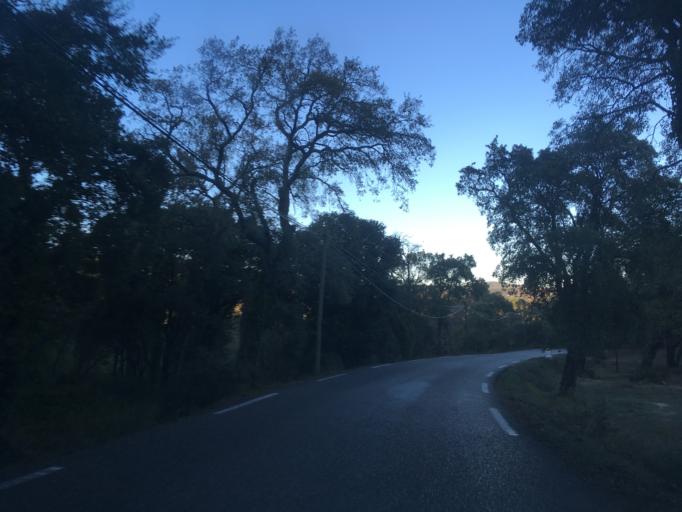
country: FR
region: Provence-Alpes-Cote d'Azur
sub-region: Departement du Var
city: Le Plan-de-la-Tour
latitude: 43.3168
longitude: 6.5403
